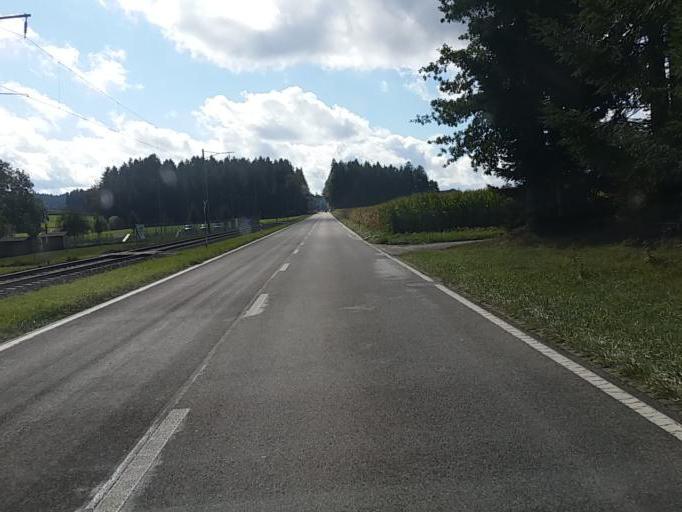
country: CH
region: Bern
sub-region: Emmental District
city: Sumiswald
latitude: 47.0687
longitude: 7.7484
